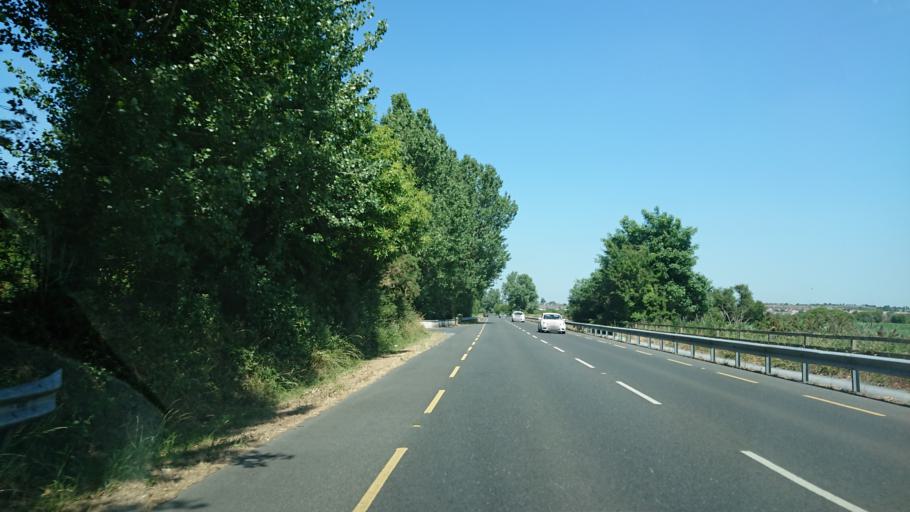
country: IE
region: Munster
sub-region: Waterford
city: Waterford
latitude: 52.2276
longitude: -7.1243
